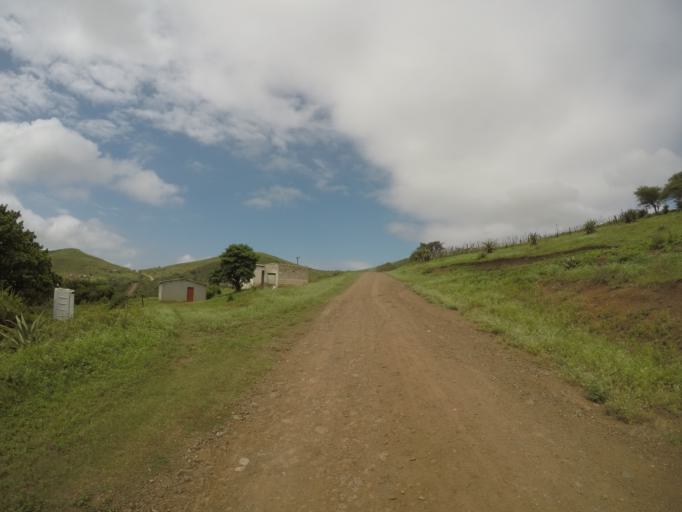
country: ZA
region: KwaZulu-Natal
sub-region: uThungulu District Municipality
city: Empangeni
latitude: -28.6268
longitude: 31.8700
